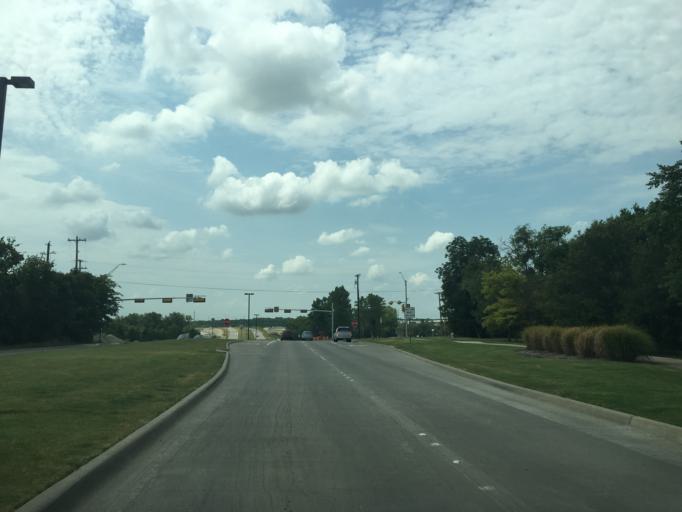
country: US
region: Texas
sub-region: Rockwall County
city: Rockwall
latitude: 32.9442
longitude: -96.4424
